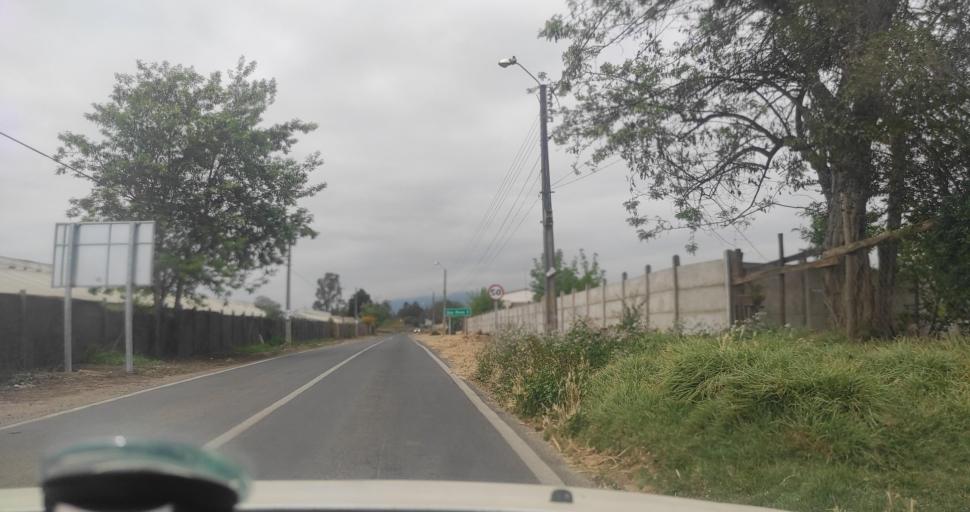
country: CL
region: Valparaiso
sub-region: Provincia de Marga Marga
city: Limache
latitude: -33.0141
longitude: -71.2427
